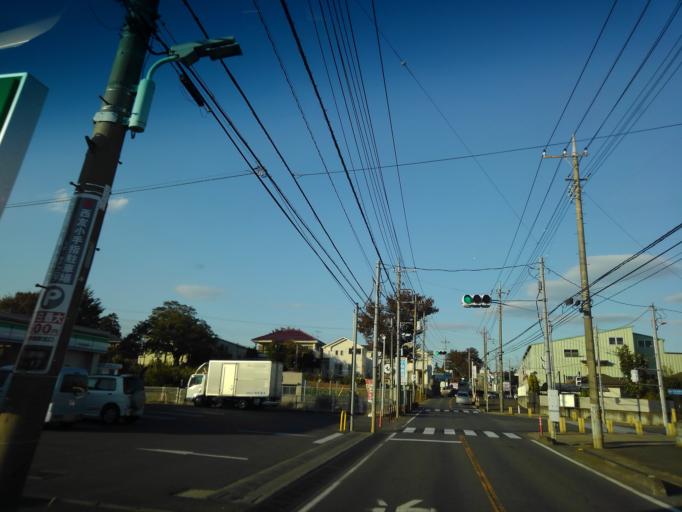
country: JP
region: Saitama
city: Tokorozawa
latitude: 35.7850
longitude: 139.4265
